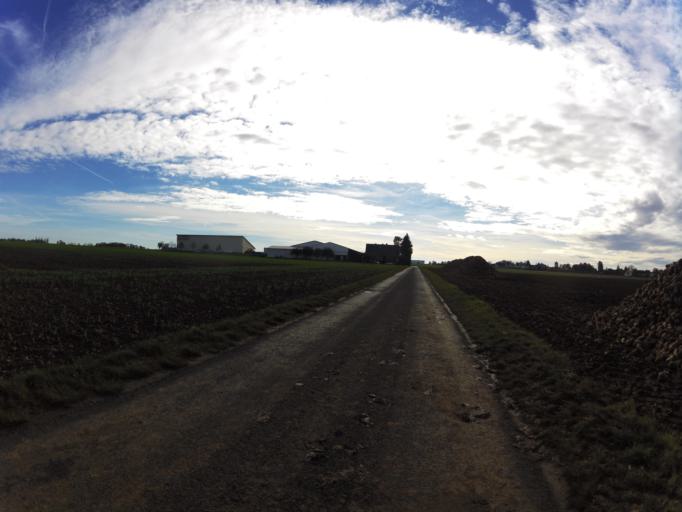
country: DE
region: Bavaria
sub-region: Regierungsbezirk Unterfranken
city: Giebelstadt
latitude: 49.6595
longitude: 9.9532
